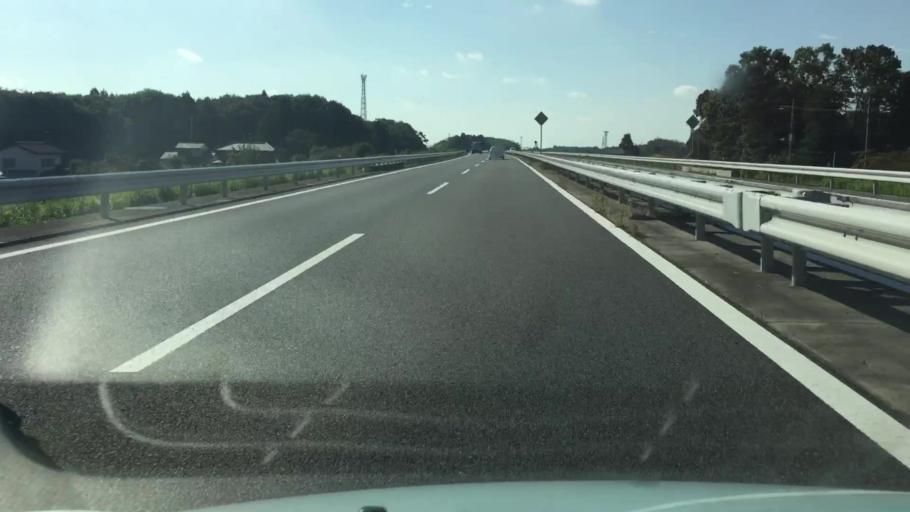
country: JP
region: Tochigi
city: Mooka
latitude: 36.5025
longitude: 139.9885
